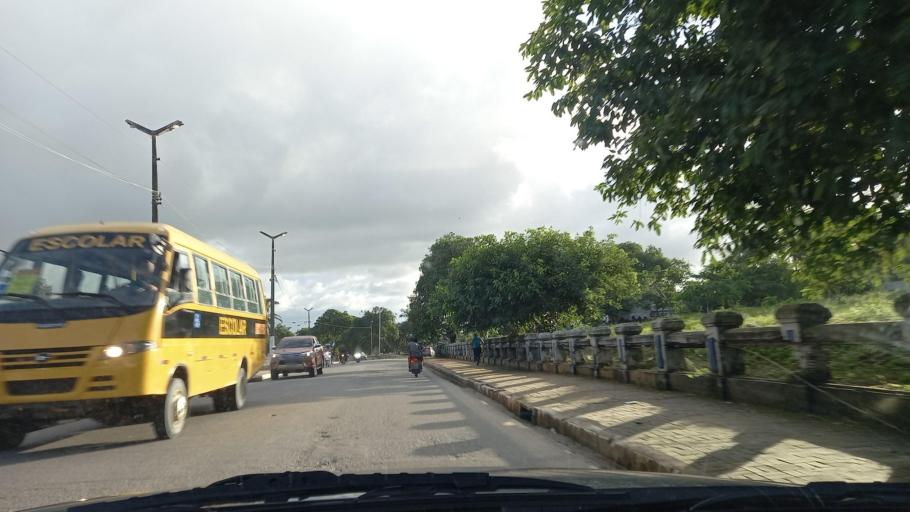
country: BR
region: Pernambuco
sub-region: Palmares
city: Palmares
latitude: -8.6812
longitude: -35.5845
